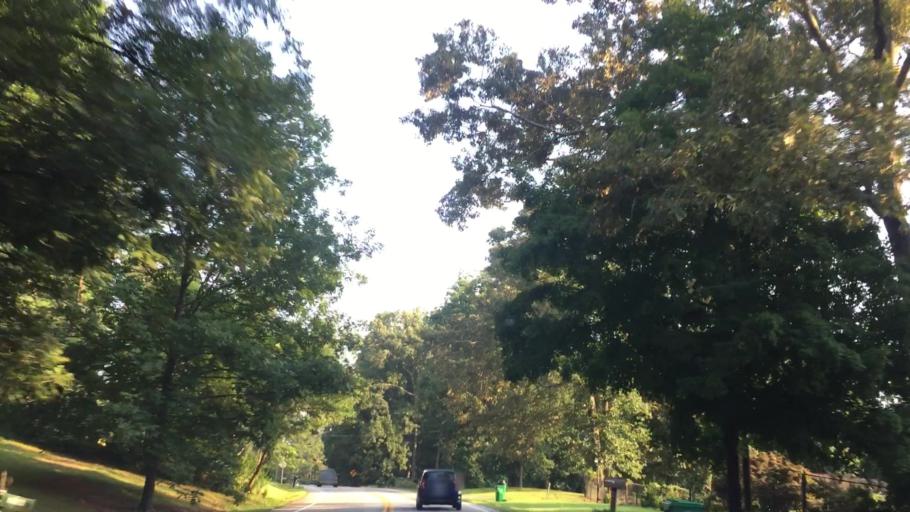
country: US
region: Georgia
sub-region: DeKalb County
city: Pine Mountain
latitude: 33.6753
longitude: -84.1960
